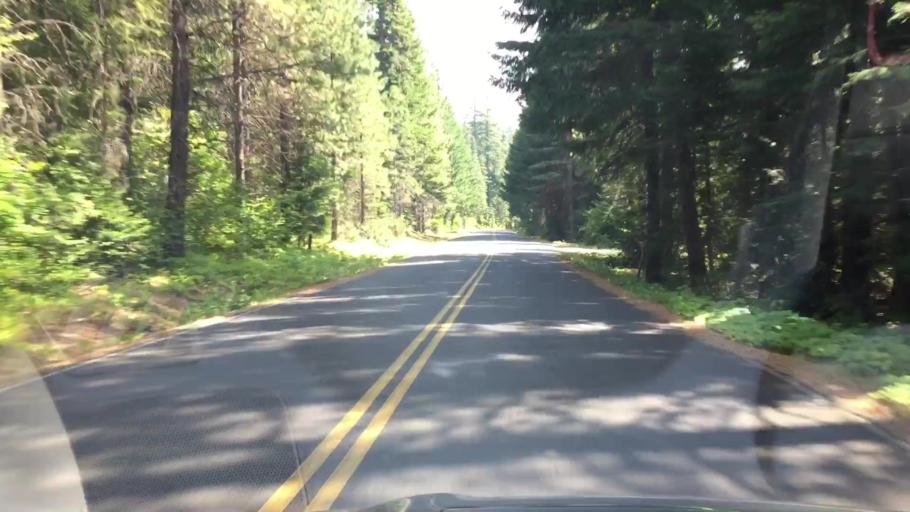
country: US
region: Washington
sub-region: Klickitat County
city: White Salmon
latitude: 46.0715
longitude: -121.5784
